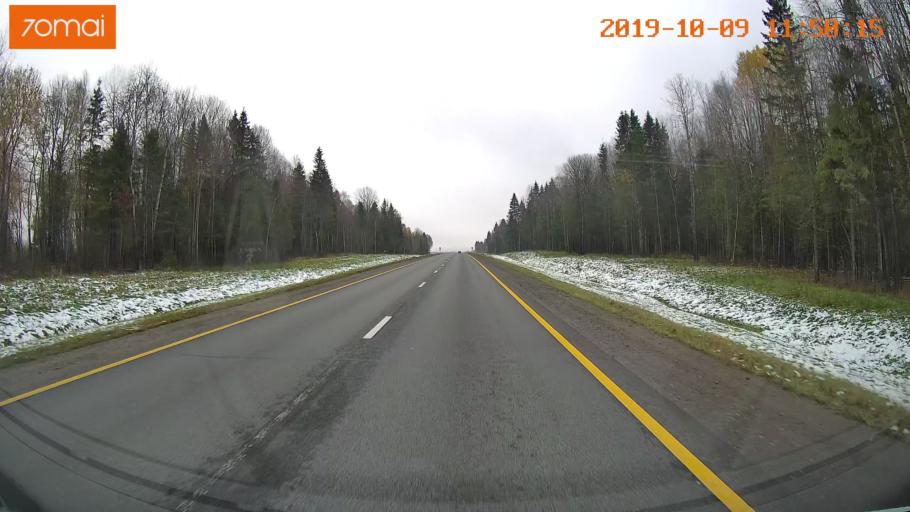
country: RU
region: Vologda
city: Gryazovets
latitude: 58.8078
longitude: 40.2435
